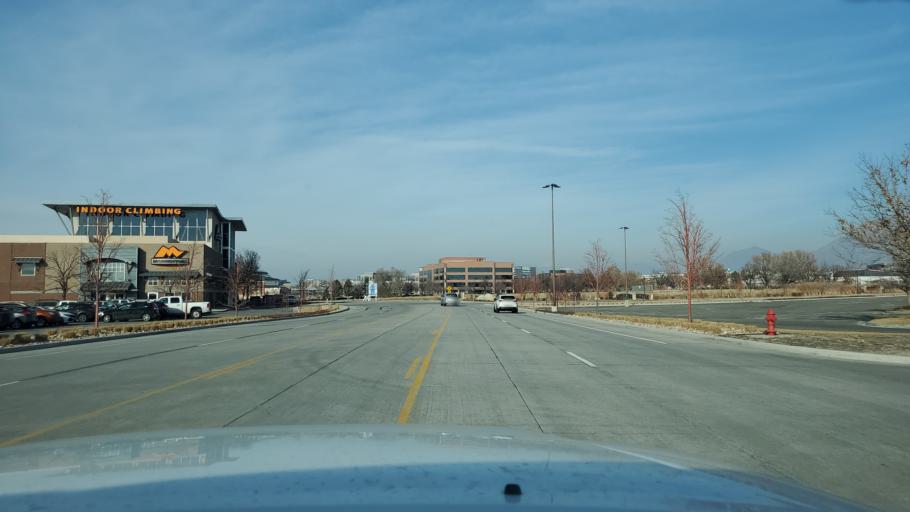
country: US
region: Utah
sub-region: Salt Lake County
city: Sandy City
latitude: 40.5633
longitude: -111.8977
